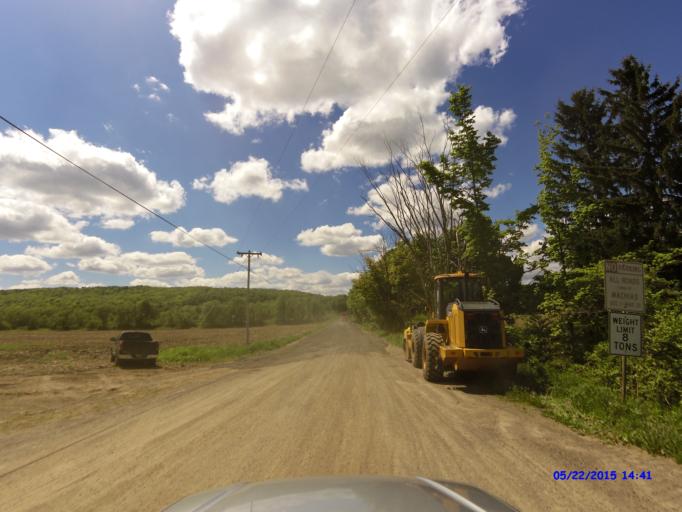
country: US
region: New York
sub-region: Cattaraugus County
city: Franklinville
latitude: 42.3504
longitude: -78.5491
